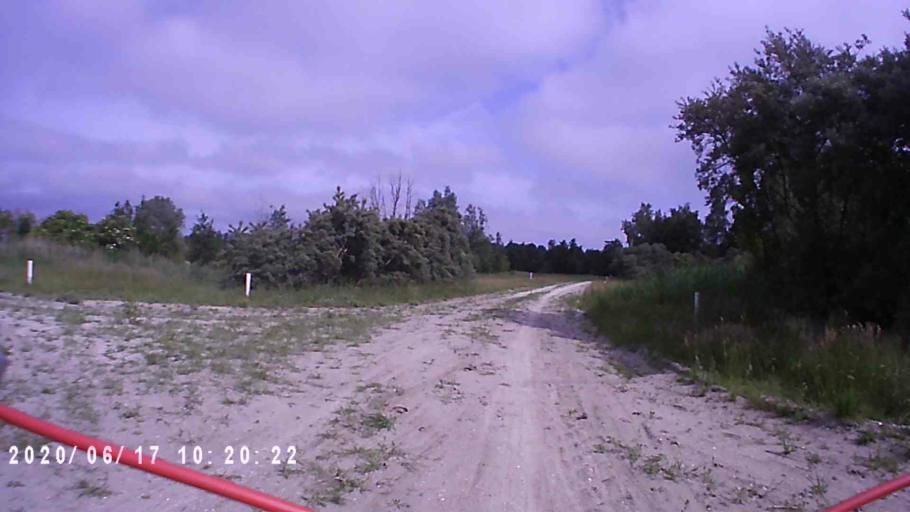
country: NL
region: Groningen
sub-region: Gemeente De Marne
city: Ulrum
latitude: 53.3896
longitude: 6.2483
